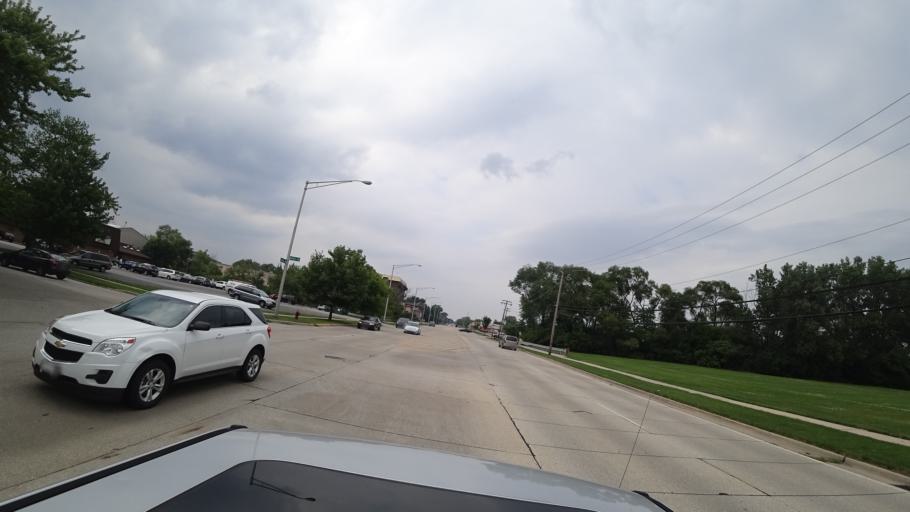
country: US
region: Illinois
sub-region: Cook County
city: Oak Lawn
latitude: 41.7014
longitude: -87.7596
